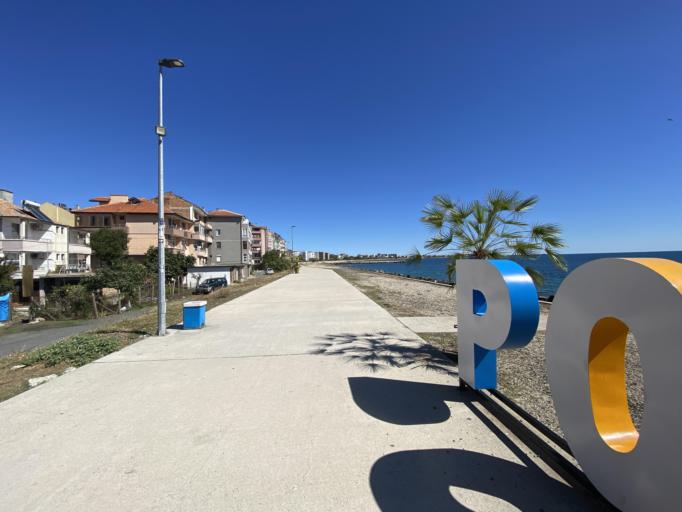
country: BG
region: Burgas
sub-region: Obshtina Pomorie
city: Pomorie
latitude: 42.5650
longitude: 27.6133
